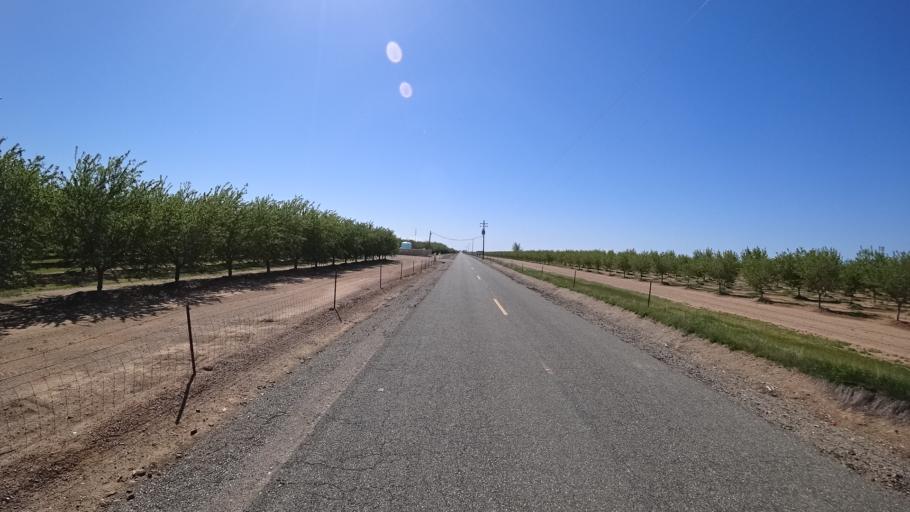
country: US
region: California
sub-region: Glenn County
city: Orland
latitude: 39.6651
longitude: -122.2531
